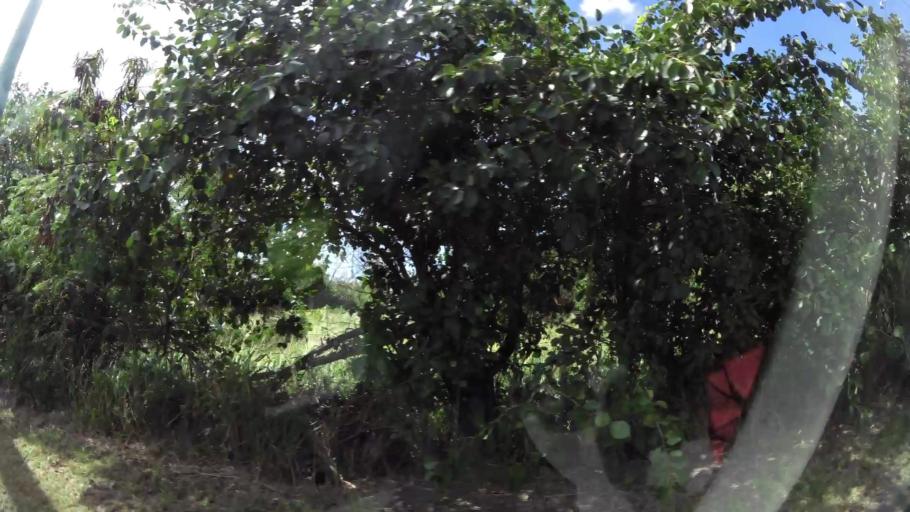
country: KN
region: Saint Thomas Lowland
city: Cotton Ground
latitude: 17.1695
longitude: -62.6247
